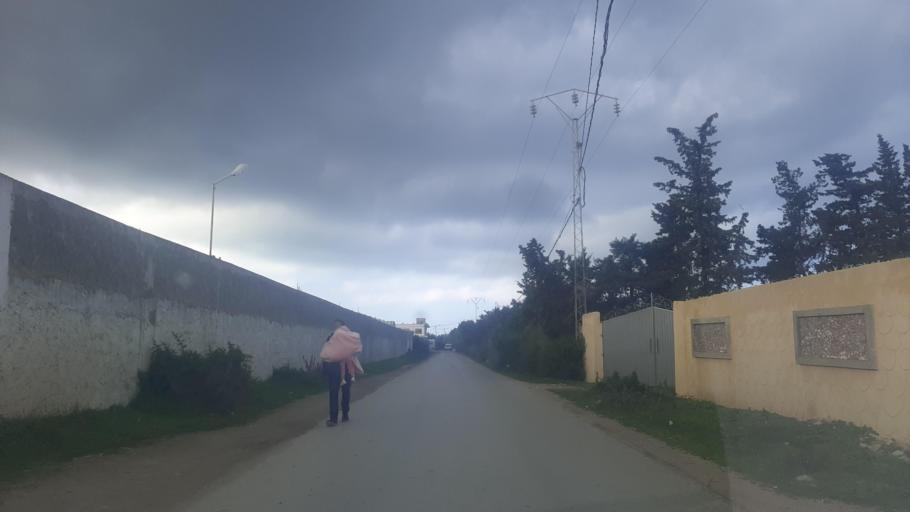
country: TN
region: Nabul
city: Manzil Bu Zalafah
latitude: 36.7323
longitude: 10.5375
